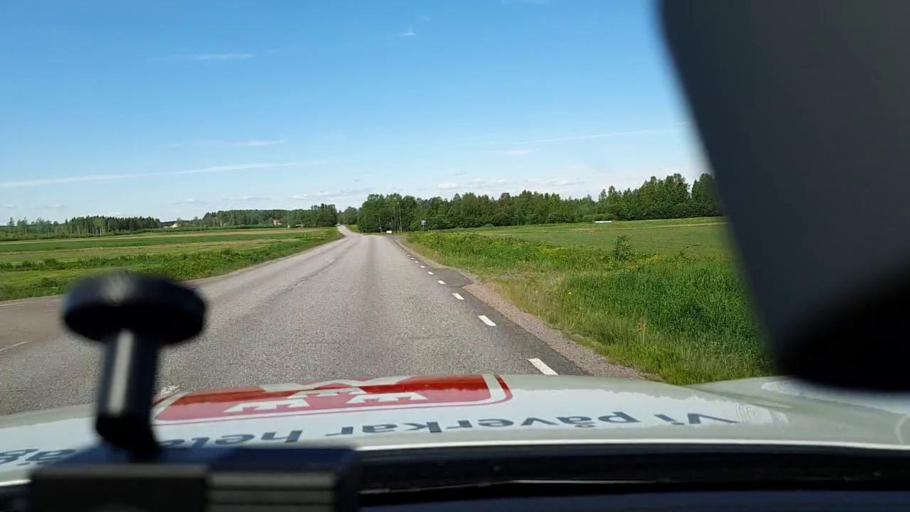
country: SE
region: Norrbotten
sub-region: Lulea Kommun
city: Sodra Sunderbyn
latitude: 65.6516
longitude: 21.8660
